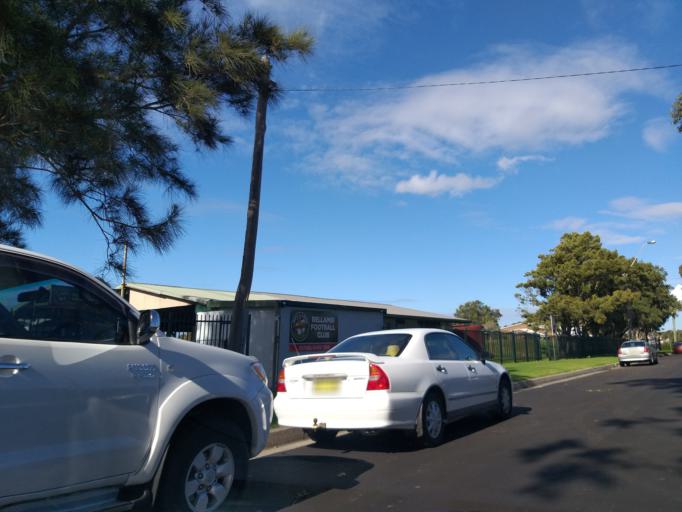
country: AU
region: New South Wales
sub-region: Wollongong
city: East Corrimal
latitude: -34.3672
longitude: 150.9169
